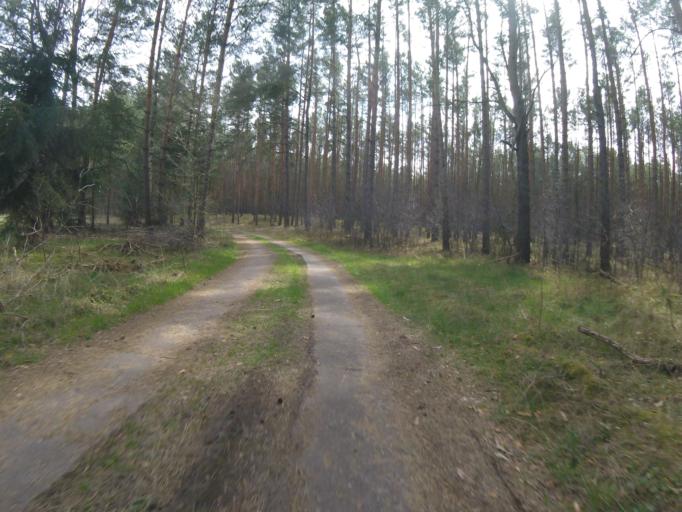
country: DE
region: Brandenburg
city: Schwerin
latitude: 52.1783
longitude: 13.6358
